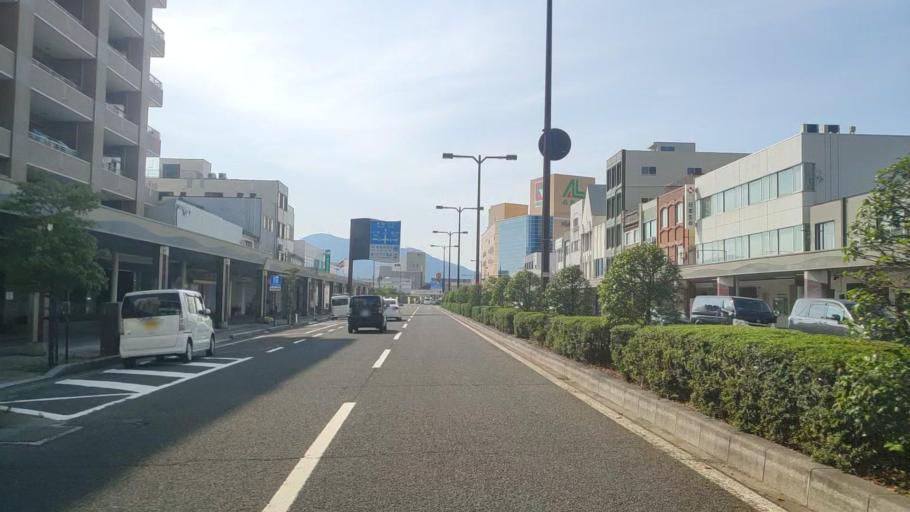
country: JP
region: Fukui
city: Tsuruga
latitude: 35.6465
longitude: 136.0737
